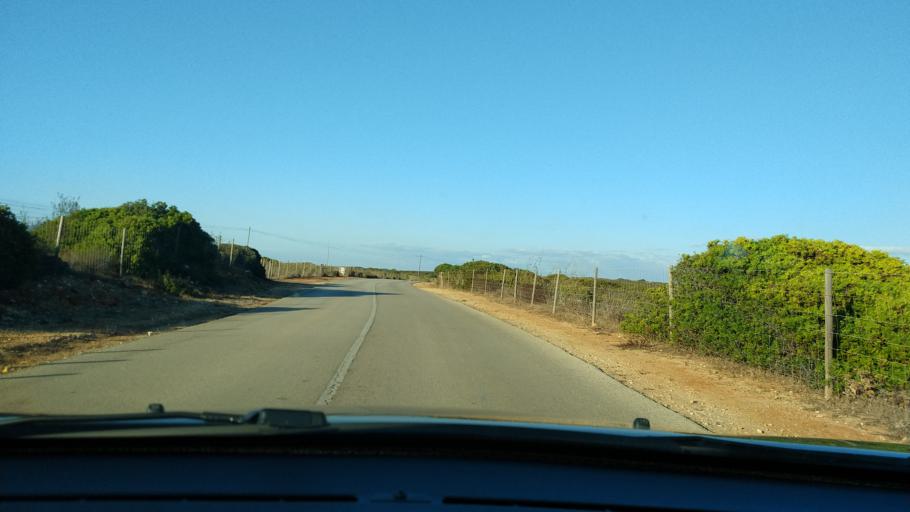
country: PT
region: Faro
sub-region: Vila do Bispo
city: Sagres
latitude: 37.0224
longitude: -8.9337
